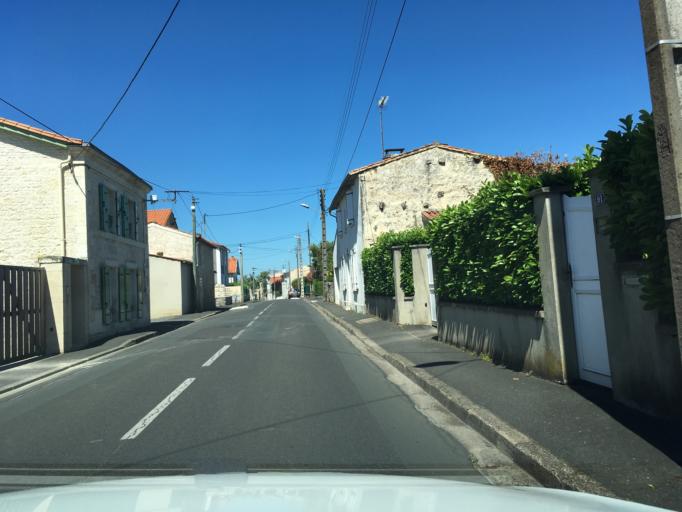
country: FR
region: Poitou-Charentes
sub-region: Departement des Deux-Sevres
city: Niort
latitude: 46.3264
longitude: -0.4392
